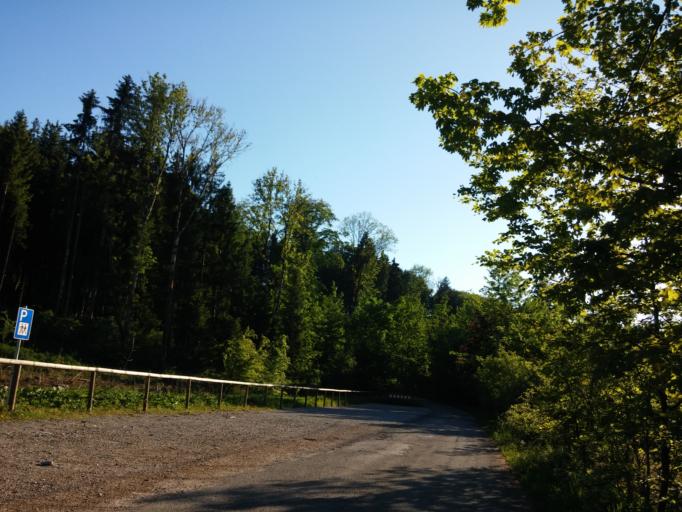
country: DE
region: Bavaria
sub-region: Swabia
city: Kronburg
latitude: 47.8679
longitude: 10.1777
